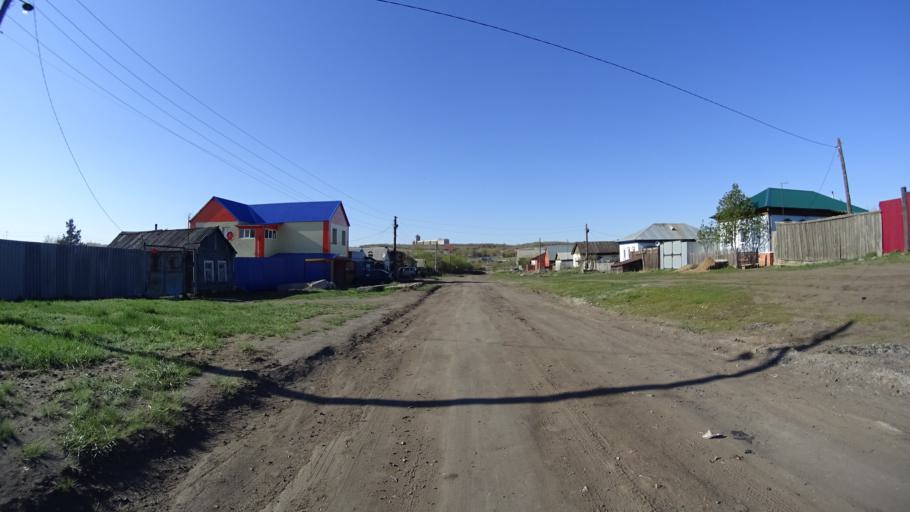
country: RU
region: Chelyabinsk
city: Troitsk
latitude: 54.0922
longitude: 61.5999
